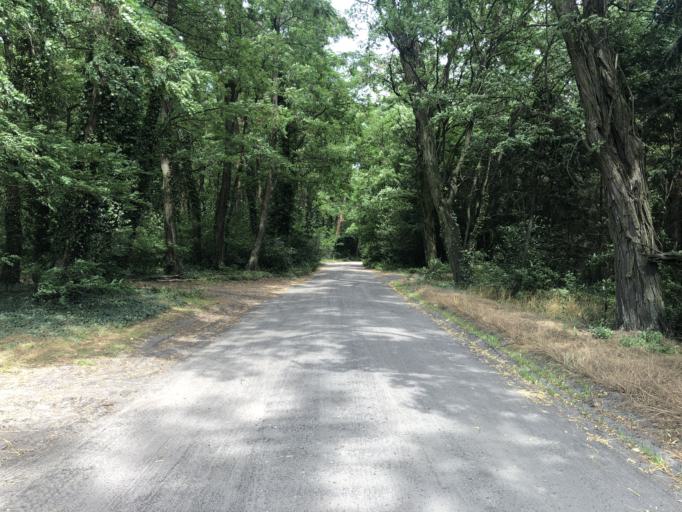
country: PL
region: Greater Poland Voivodeship
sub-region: Powiat leszczynski
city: Swieciechowa
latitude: 51.8984
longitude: 16.4365
